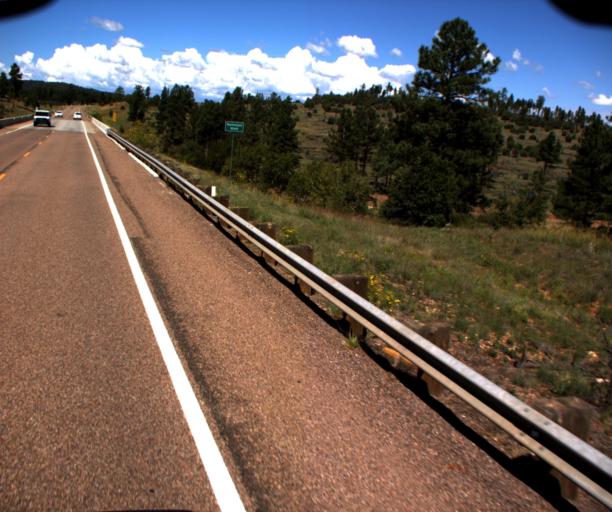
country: US
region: Arizona
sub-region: Navajo County
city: Linden
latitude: 34.3113
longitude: -110.2274
